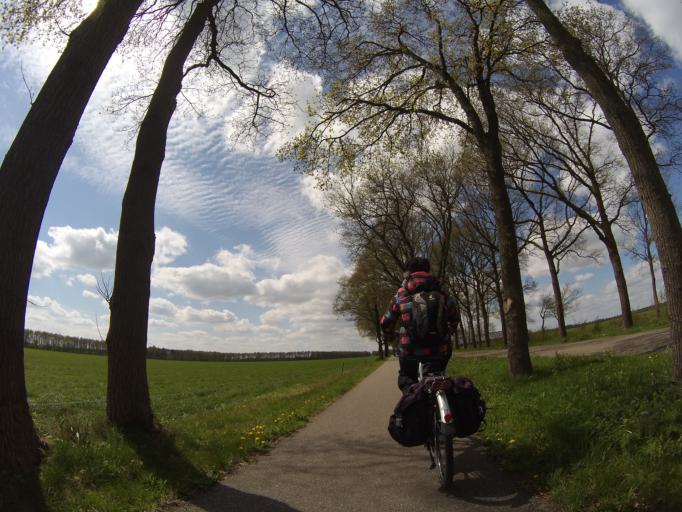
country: NL
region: Drenthe
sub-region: Gemeente Coevorden
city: Sleen
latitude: 52.7721
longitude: 6.7913
